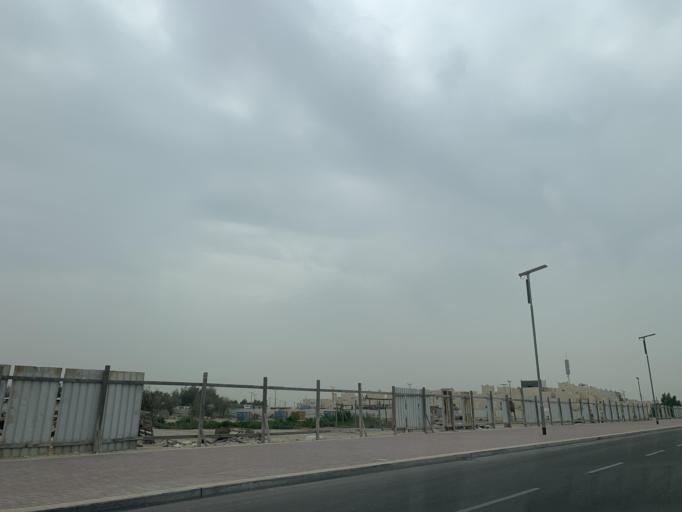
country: BH
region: Northern
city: Madinat `Isa
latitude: 26.1693
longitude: 50.5153
